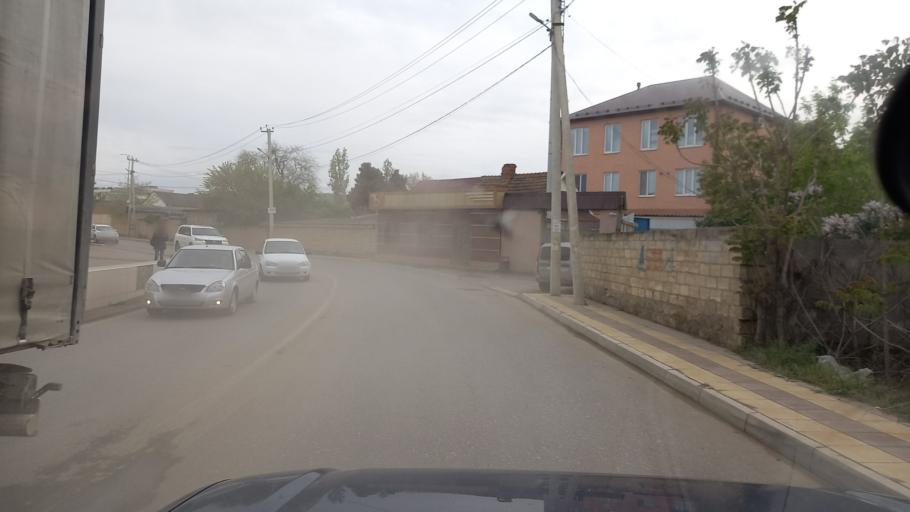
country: RU
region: Dagestan
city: Derbent
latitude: 42.0630
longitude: 48.3039
